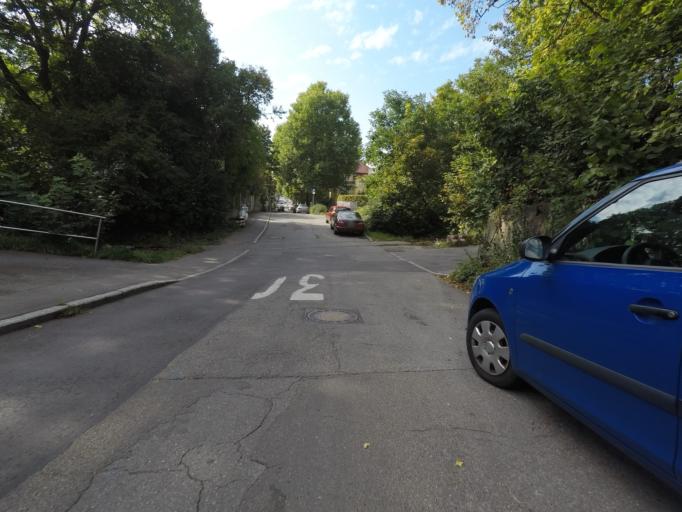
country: DE
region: Baden-Wuerttemberg
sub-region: Tuebingen Region
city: Reutlingen
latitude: 48.4918
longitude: 9.2272
